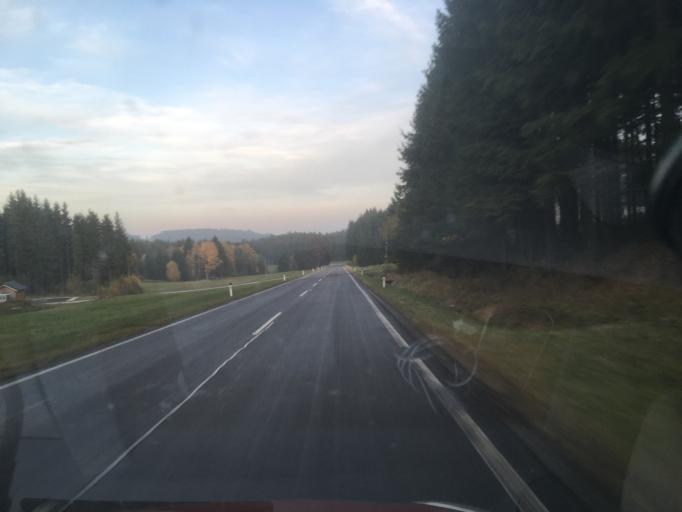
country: AT
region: Lower Austria
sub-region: Politischer Bezirk Zwettl
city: Langschlag
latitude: 48.5782
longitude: 14.8002
